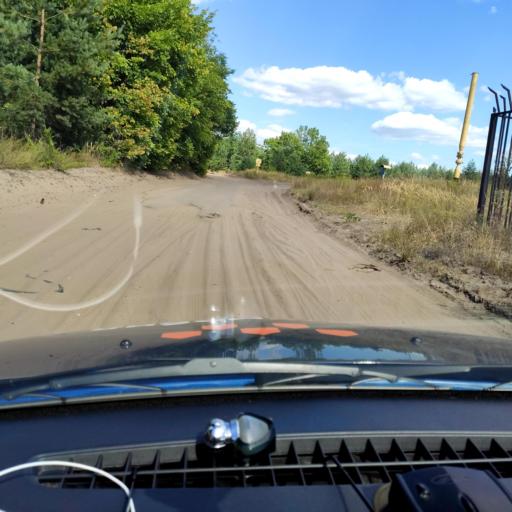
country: RU
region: Voronezj
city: Somovo
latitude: 51.7156
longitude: 39.3734
